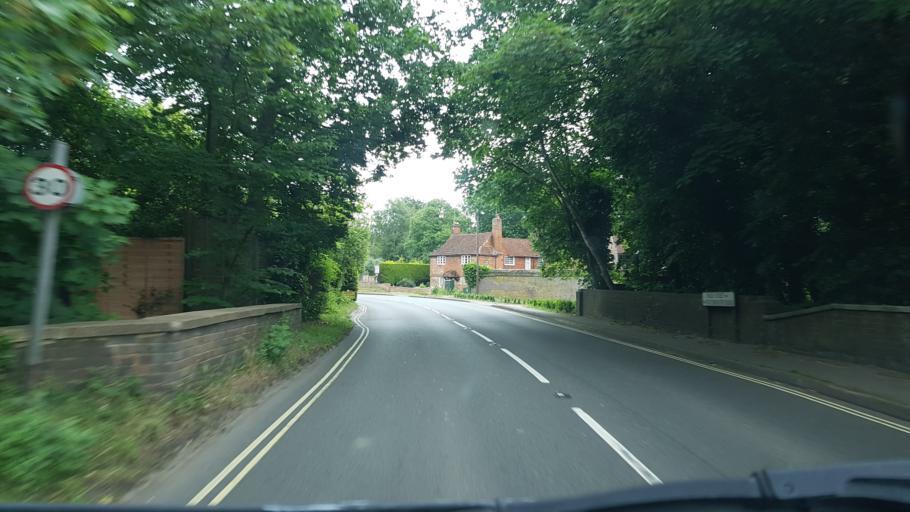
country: GB
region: England
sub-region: Surrey
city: Ripley
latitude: 51.3020
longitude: -0.4861
